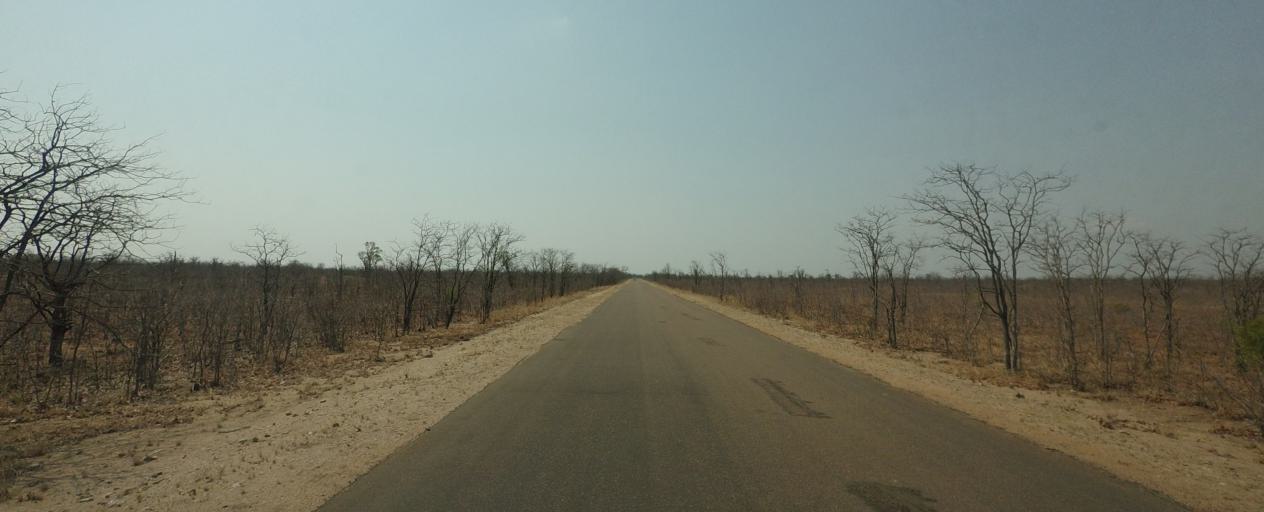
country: ZA
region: Limpopo
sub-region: Mopani District Municipality
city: Giyani
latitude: -23.3591
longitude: 31.3192
